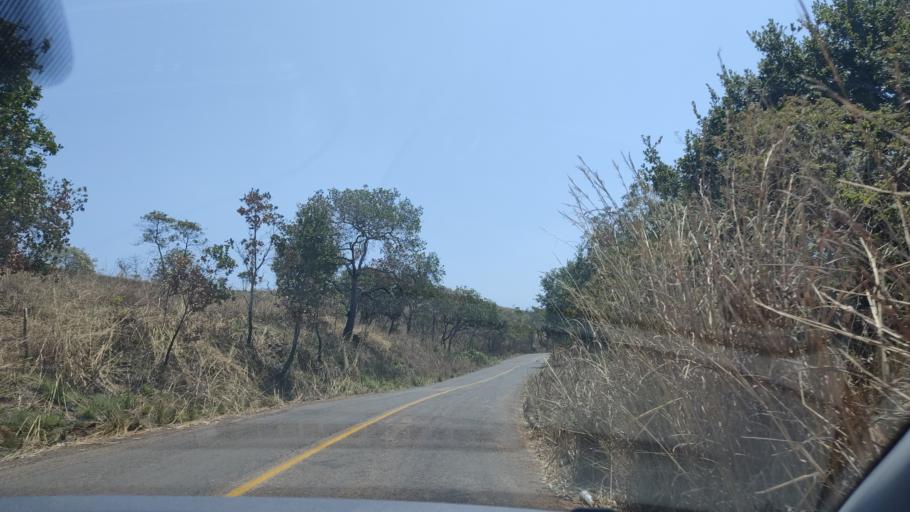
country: MX
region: Nayarit
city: Puga
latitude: 21.5777
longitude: -104.7623
